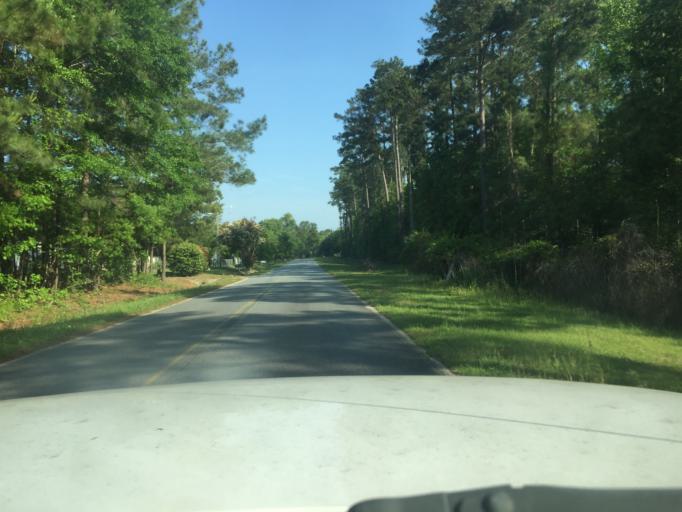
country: US
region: Georgia
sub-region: Chatham County
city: Georgetown
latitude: 32.0327
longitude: -81.2128
